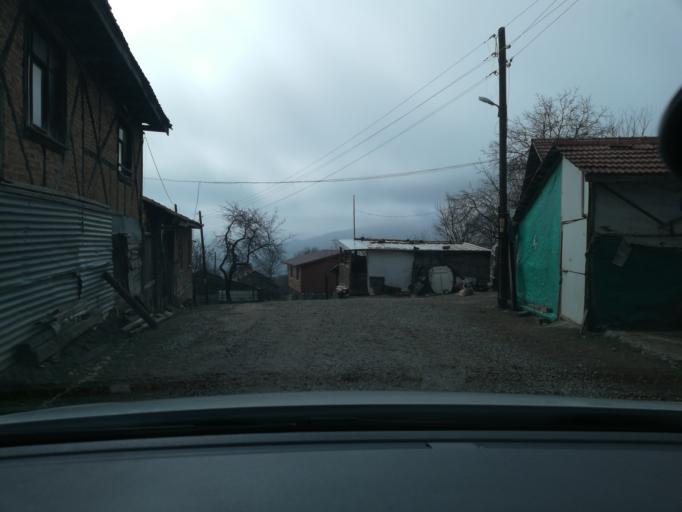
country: TR
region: Bolu
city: Bolu
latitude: 40.6684
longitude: 31.4599
